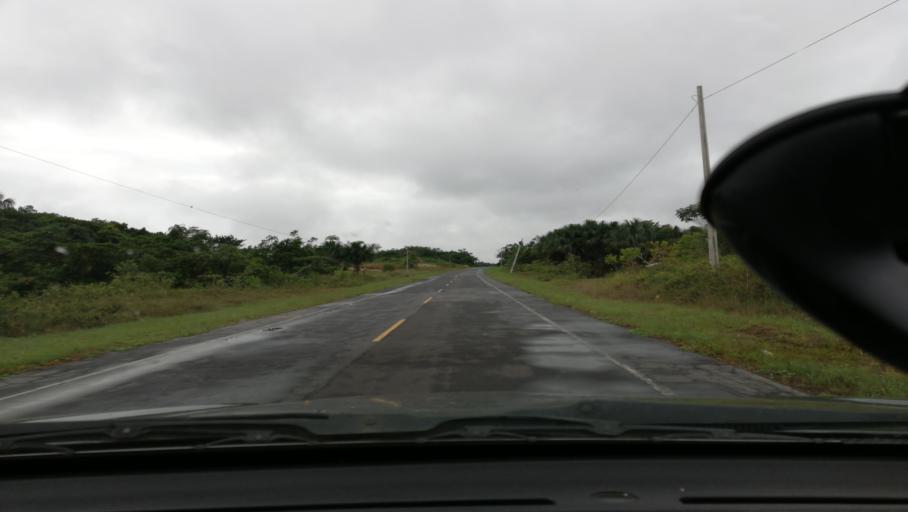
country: PE
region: Loreto
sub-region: Provincia de Loreto
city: Nauta
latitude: -4.3374
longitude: -73.5366
